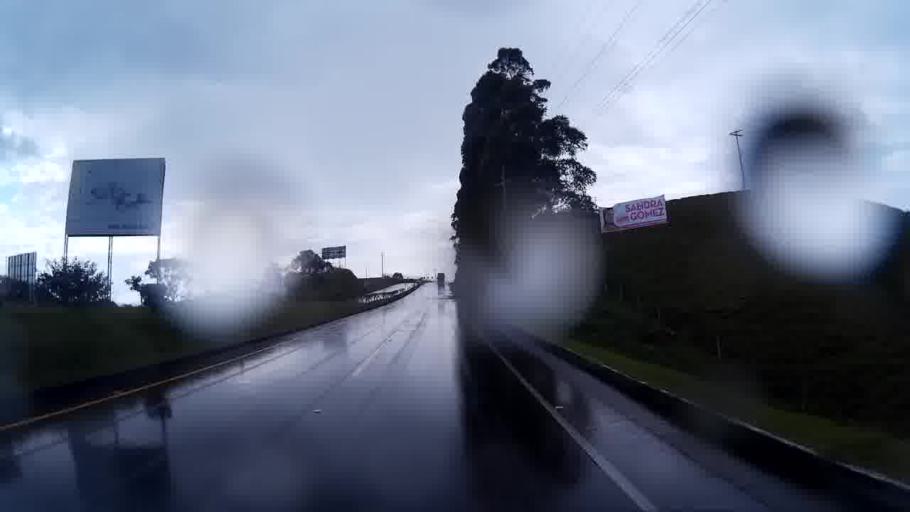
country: CO
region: Quindio
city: Salento
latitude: 4.6765
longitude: -75.6014
